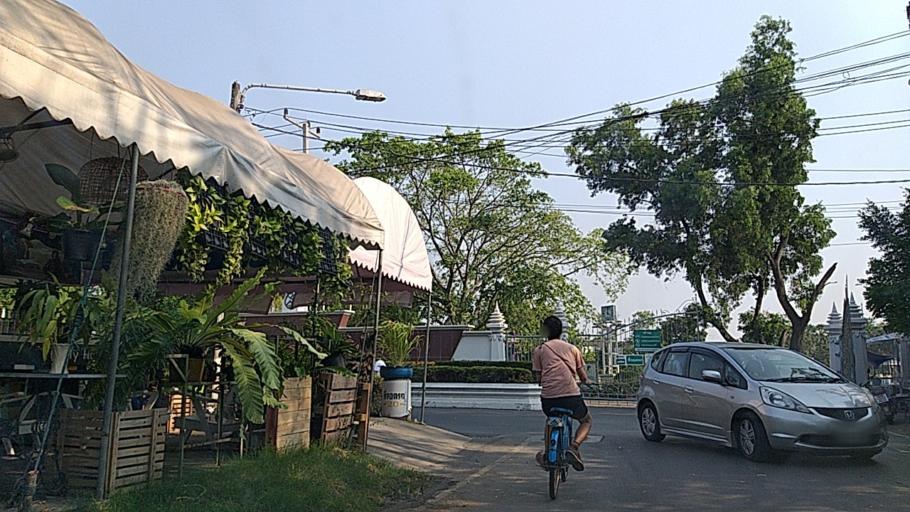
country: TH
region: Bangkok
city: Don Mueang
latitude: 13.9328
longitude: 100.5541
